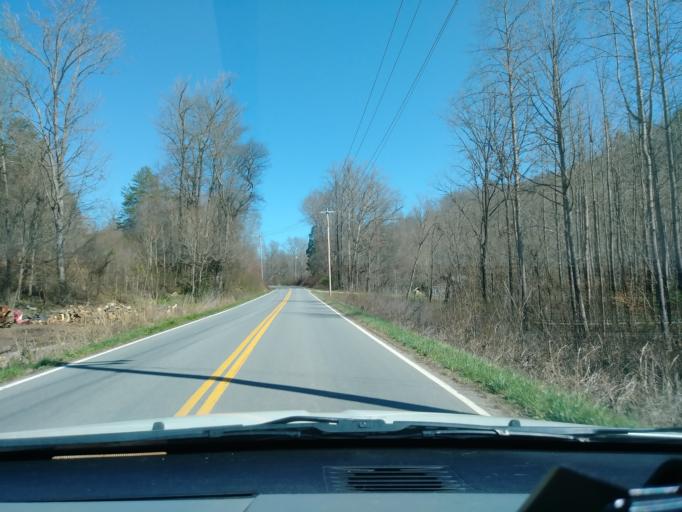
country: US
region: Tennessee
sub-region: Cocke County
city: Newport
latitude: 35.9536
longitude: -83.0514
